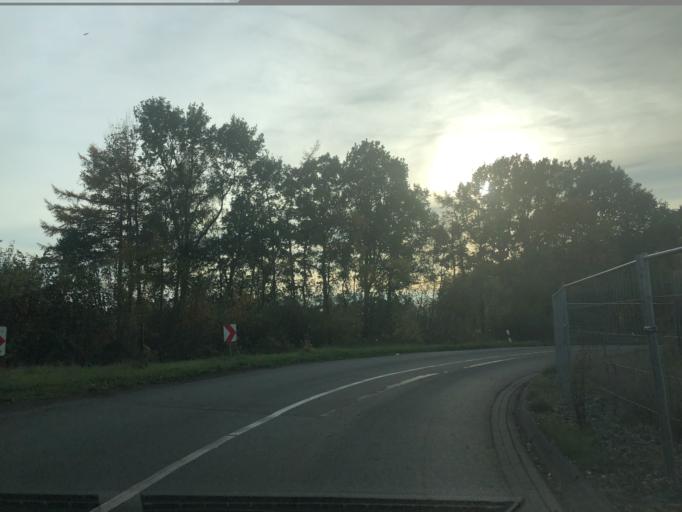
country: DE
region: Lower Saxony
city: Edewecht
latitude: 53.0828
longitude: 7.9669
